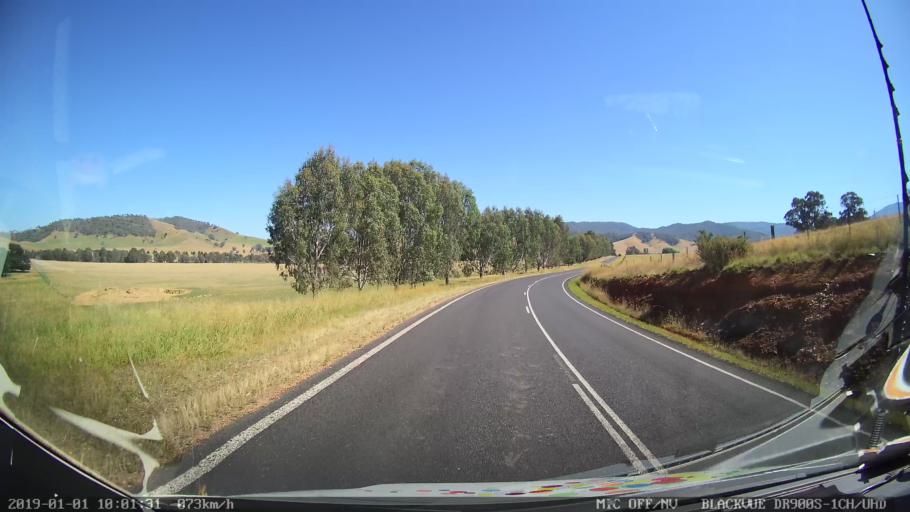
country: AU
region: New South Wales
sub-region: Snowy River
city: Jindabyne
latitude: -36.1907
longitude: 148.1006
